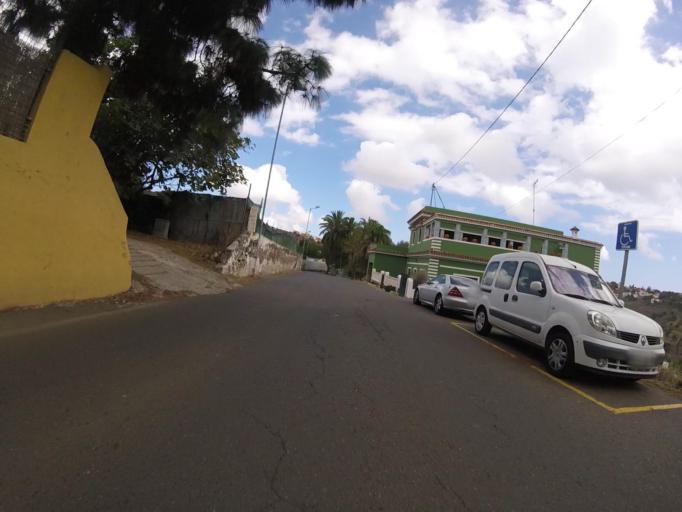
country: ES
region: Canary Islands
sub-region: Provincia de Las Palmas
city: Santa Brigida
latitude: 28.0429
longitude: -15.4888
